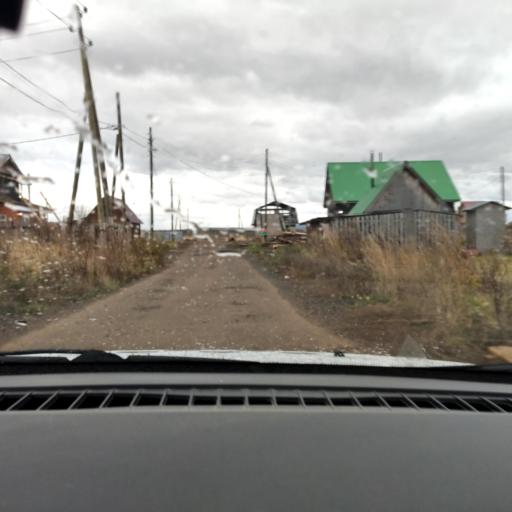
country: RU
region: Perm
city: Kultayevo
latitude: 57.8962
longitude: 55.9579
